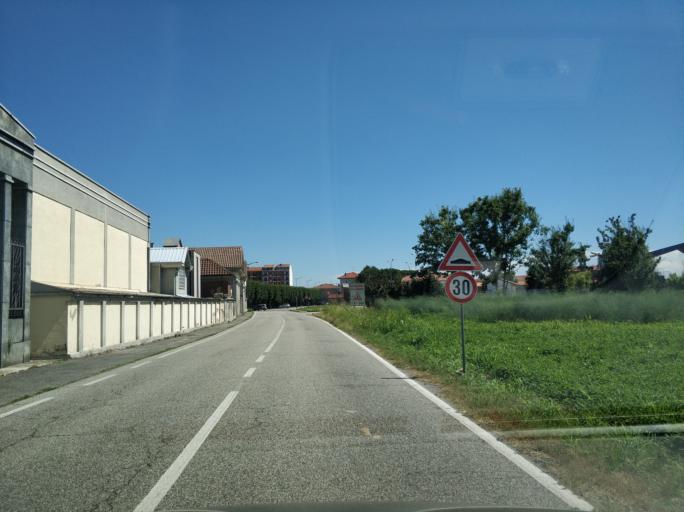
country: IT
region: Piedmont
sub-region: Provincia di Vercelli
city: Cigliano
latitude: 45.3142
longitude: 8.0212
